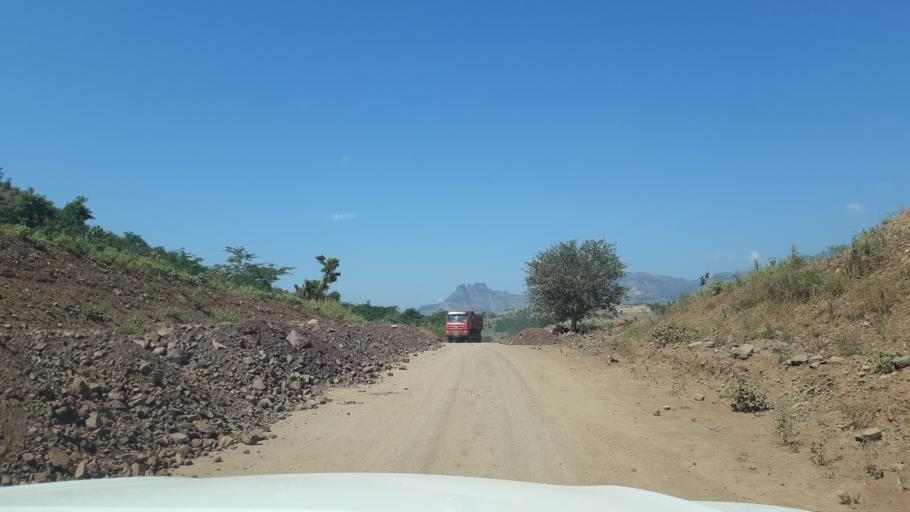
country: ET
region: Amhara
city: Dabat
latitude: 13.1931
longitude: 37.5693
